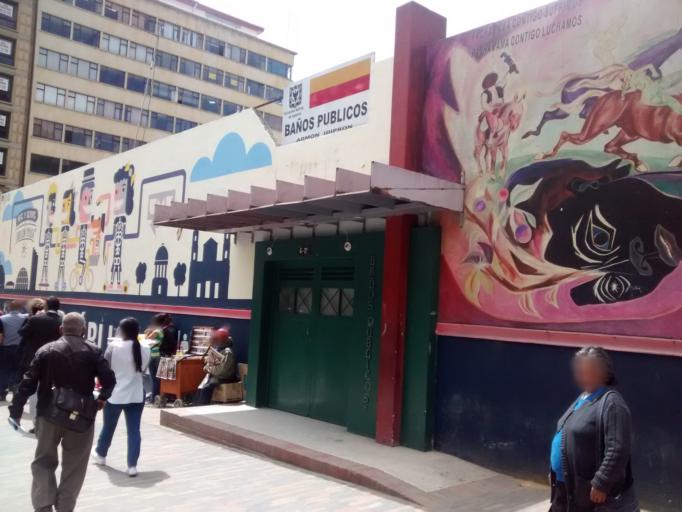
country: CO
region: Bogota D.C.
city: Bogota
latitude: 4.5992
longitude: -74.0745
